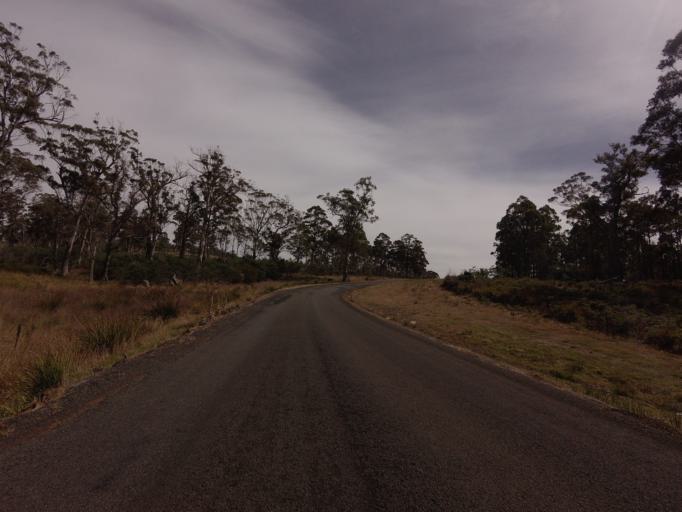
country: AU
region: Tasmania
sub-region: Sorell
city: Sorell
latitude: -42.5519
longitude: 147.6729
